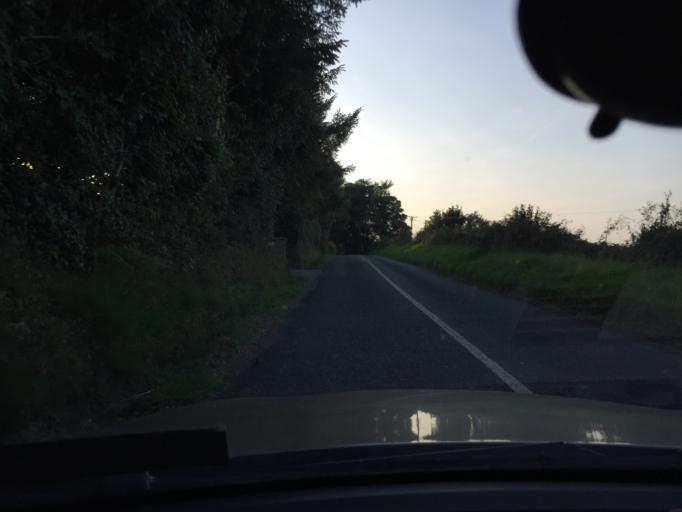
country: IE
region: Leinster
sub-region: Wicklow
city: Enniskerry
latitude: 53.1670
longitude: -6.1755
